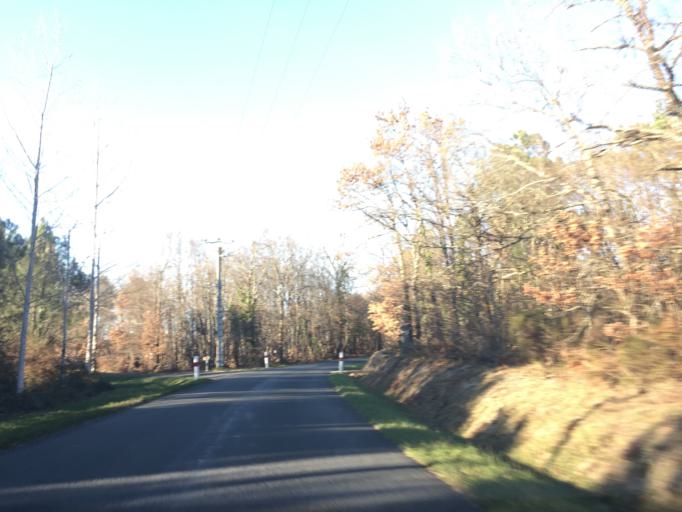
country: FR
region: Aquitaine
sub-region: Departement de la Dordogne
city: Riberac
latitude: 45.2150
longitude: 0.2948
